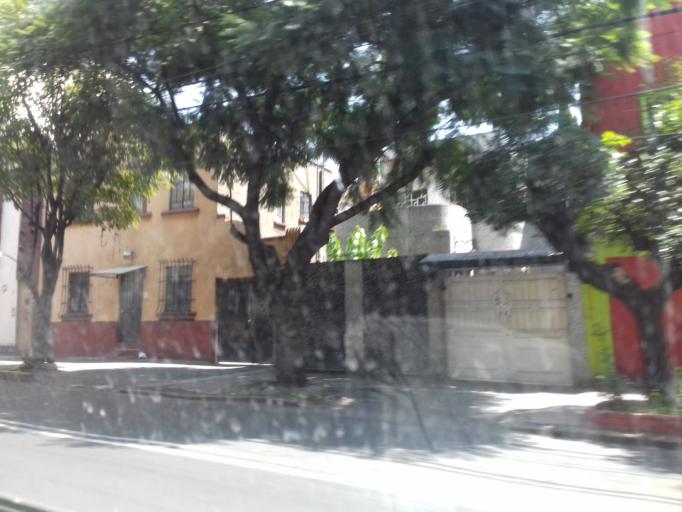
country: MX
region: Mexico City
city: Benito Juarez
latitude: 19.3972
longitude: -99.1615
